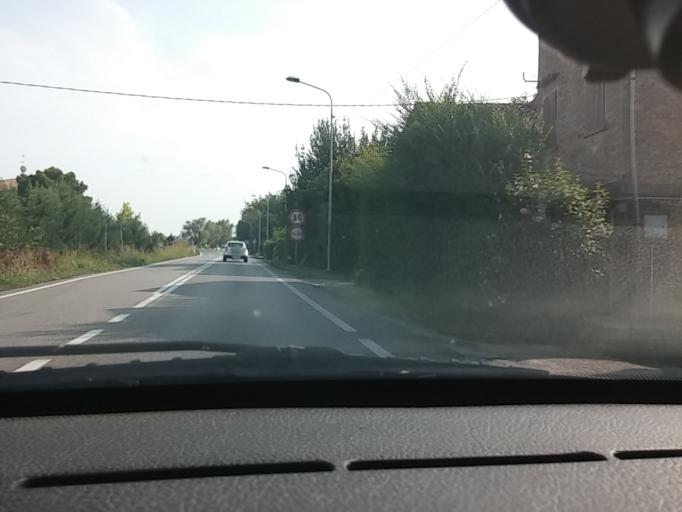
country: IT
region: Emilia-Romagna
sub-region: Provincia di Ferrara
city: Pontegradella
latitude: 44.8088
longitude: 11.6353
